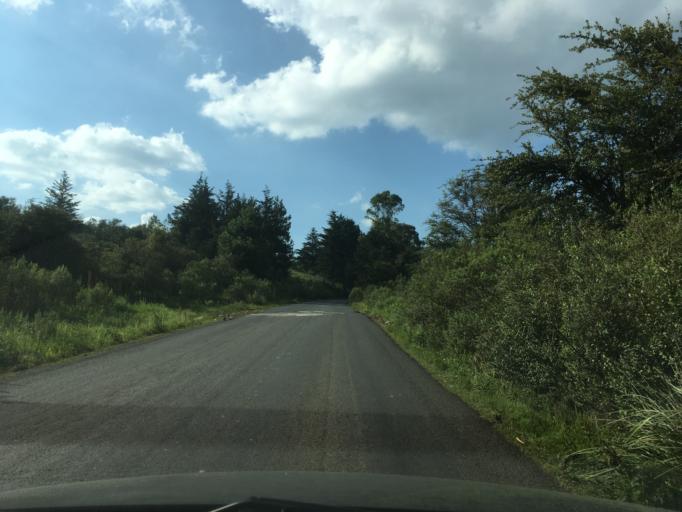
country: MX
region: Michoacan
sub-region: Nahuatzen
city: Sevina
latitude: 19.6296
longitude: -101.9276
